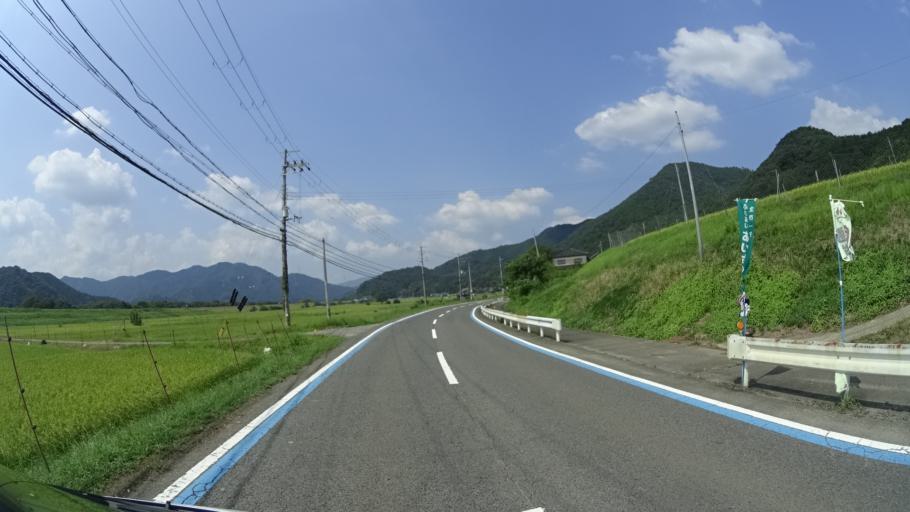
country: JP
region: Kyoto
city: Fukuchiyama
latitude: 35.3218
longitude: 135.1196
